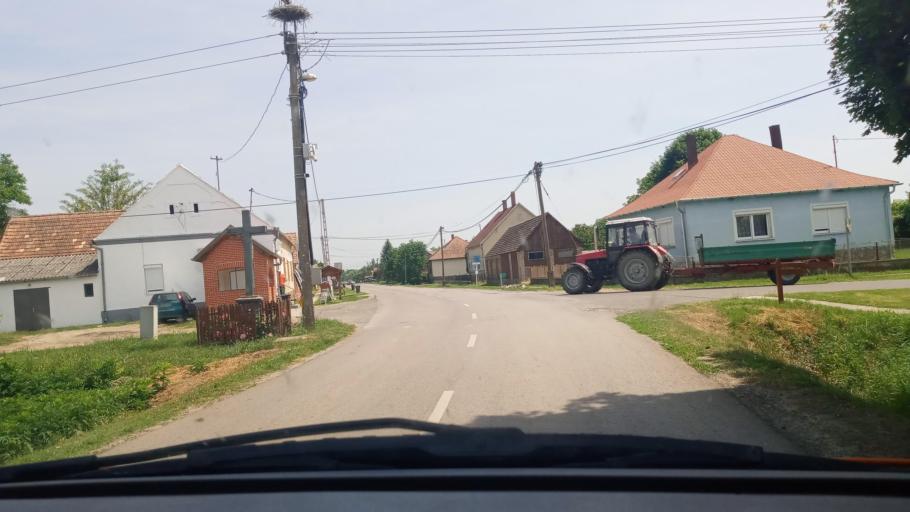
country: HU
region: Baranya
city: Szigetvar
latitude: 45.9651
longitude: 17.7095
